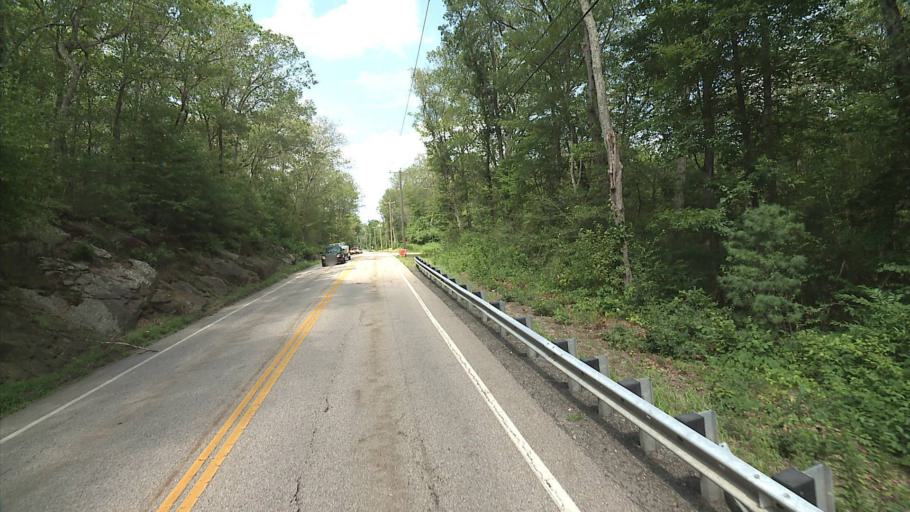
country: US
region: Connecticut
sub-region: New London County
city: Niantic
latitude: 41.3938
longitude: -72.2228
